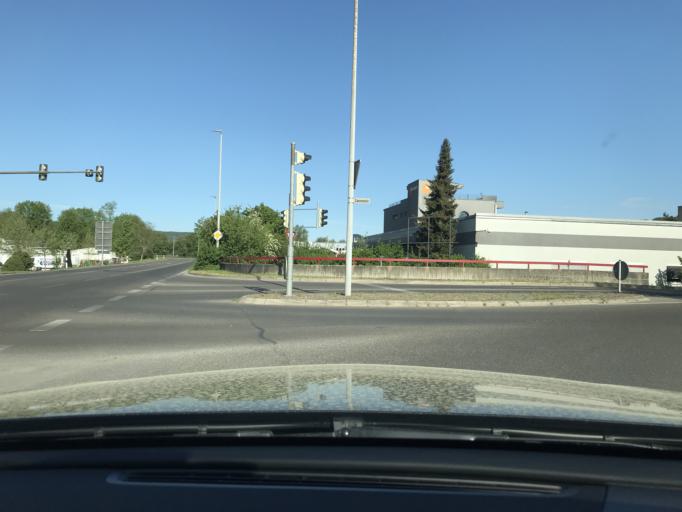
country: DE
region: Baden-Wuerttemberg
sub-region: Regierungsbezirk Stuttgart
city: Weinstadt-Endersbach
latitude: 48.8133
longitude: 9.3852
